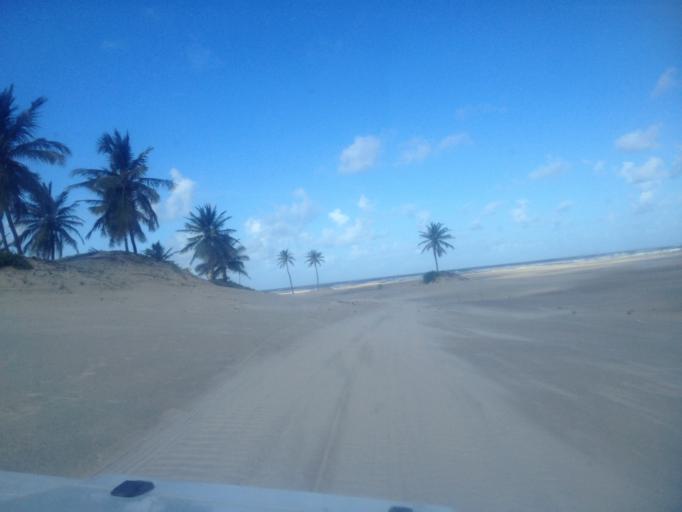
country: BR
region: Sergipe
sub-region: Indiaroba
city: Indiaroba
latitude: -11.4759
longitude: -37.3669
